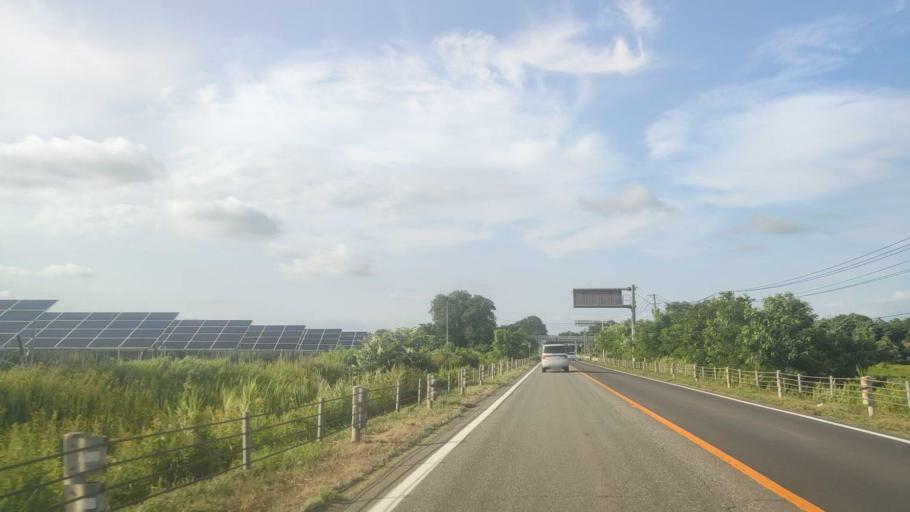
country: JP
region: Hokkaido
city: Chitose
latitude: 42.8893
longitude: 141.8125
